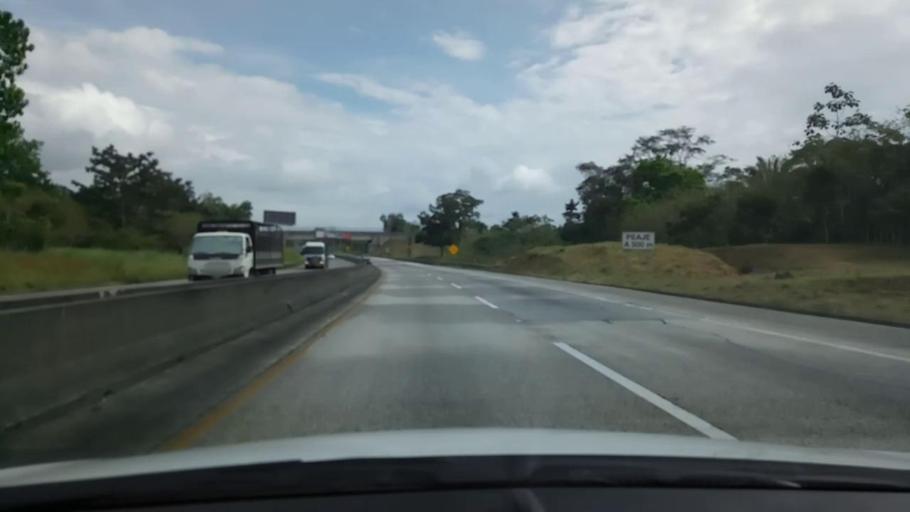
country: PA
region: Colon
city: Buena Vista
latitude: 9.2664
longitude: -79.7051
